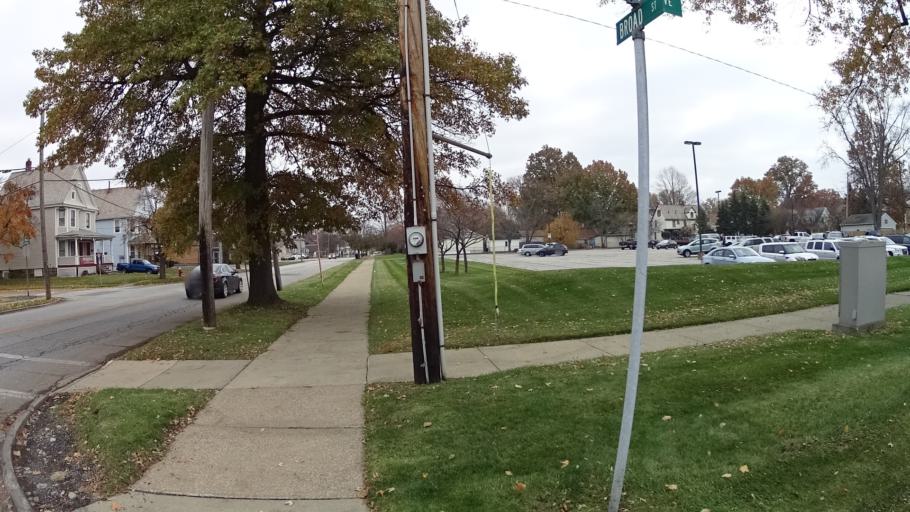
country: US
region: Ohio
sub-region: Lorain County
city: Elyria
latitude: 41.3674
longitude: -82.0948
